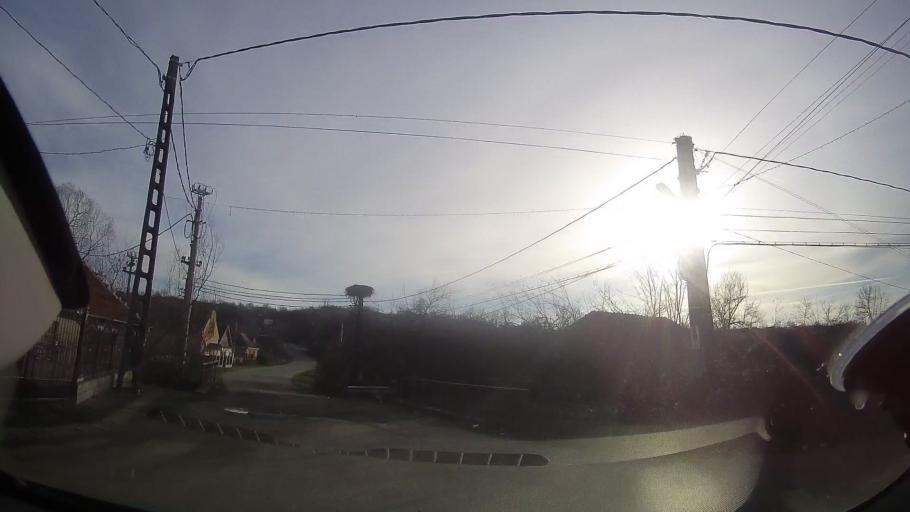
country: RO
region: Bihor
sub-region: Comuna Sarbi
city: Burzuc
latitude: 47.1078
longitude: 22.1706
